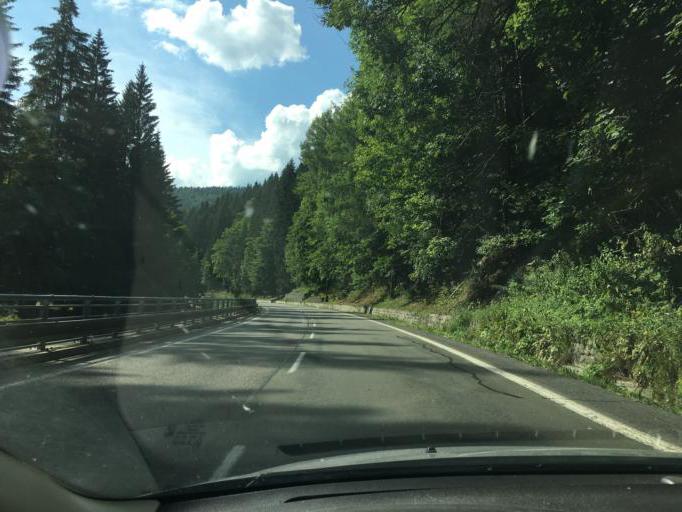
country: CZ
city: Benecko
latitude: 50.6820
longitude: 15.5874
